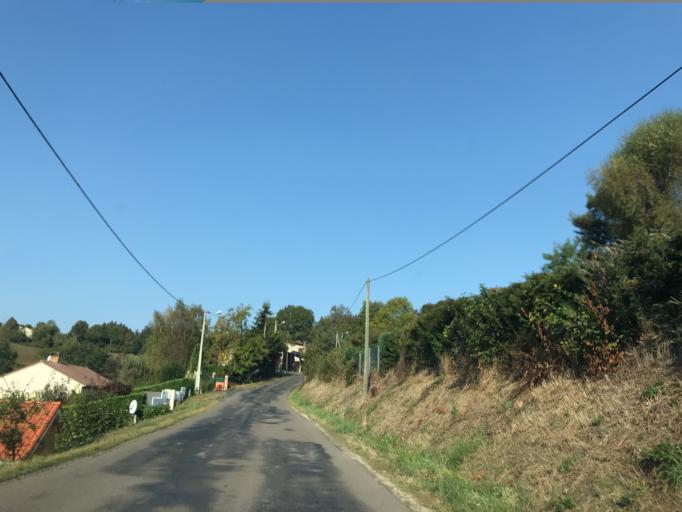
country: FR
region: Auvergne
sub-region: Departement du Puy-de-Dome
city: La Monnerie-le-Montel
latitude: 45.8816
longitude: 3.6083
